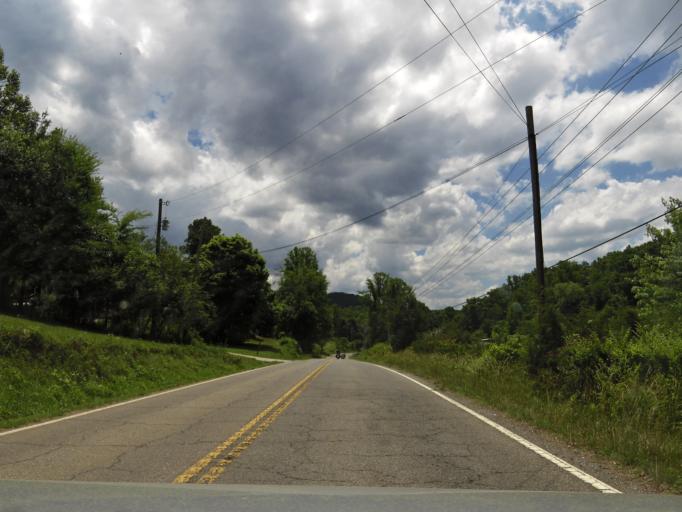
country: US
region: Tennessee
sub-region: Loudon County
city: Greenback
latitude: 35.5921
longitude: -84.0951
